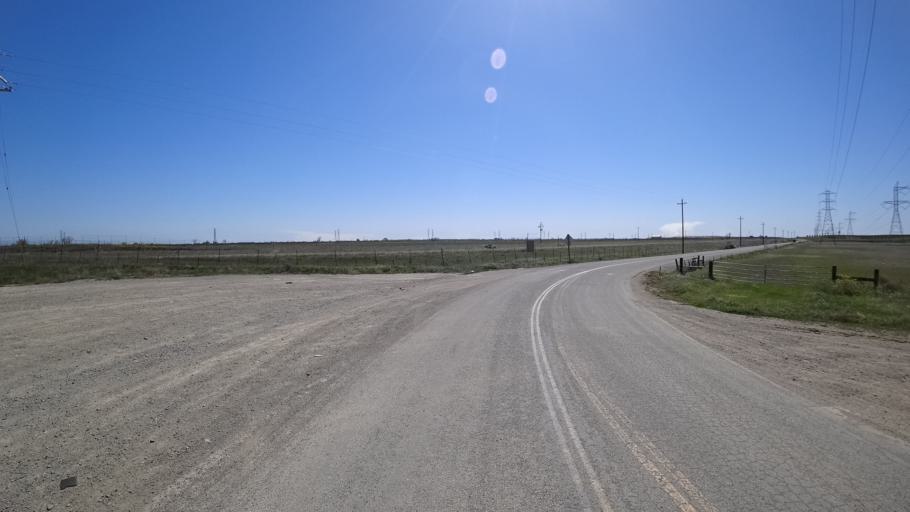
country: US
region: California
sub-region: Glenn County
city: Willows
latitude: 39.6308
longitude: -122.2732
